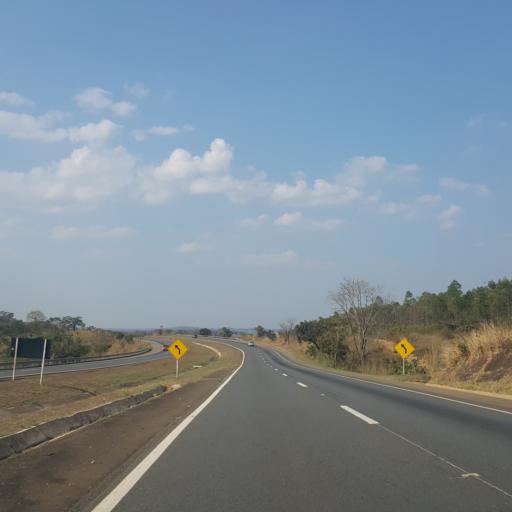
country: BR
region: Goias
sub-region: Abadiania
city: Abadiania
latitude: -16.1838
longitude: -48.6565
